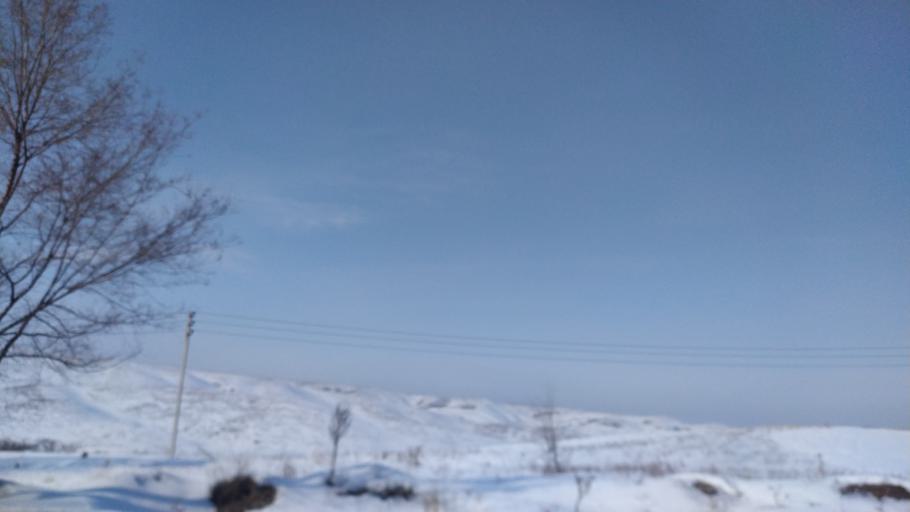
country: KZ
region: Almaty Oblysy
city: Burunday
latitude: 43.2554
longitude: 76.4637
